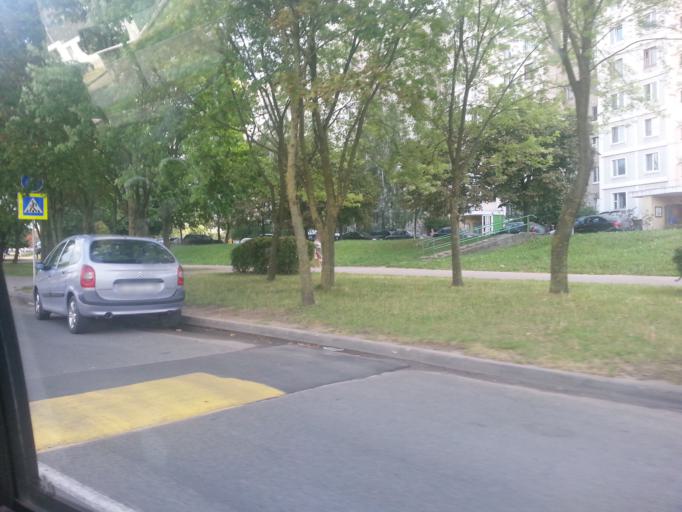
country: BY
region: Minsk
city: Novoye Medvezhino
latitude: 53.9087
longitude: 27.4531
